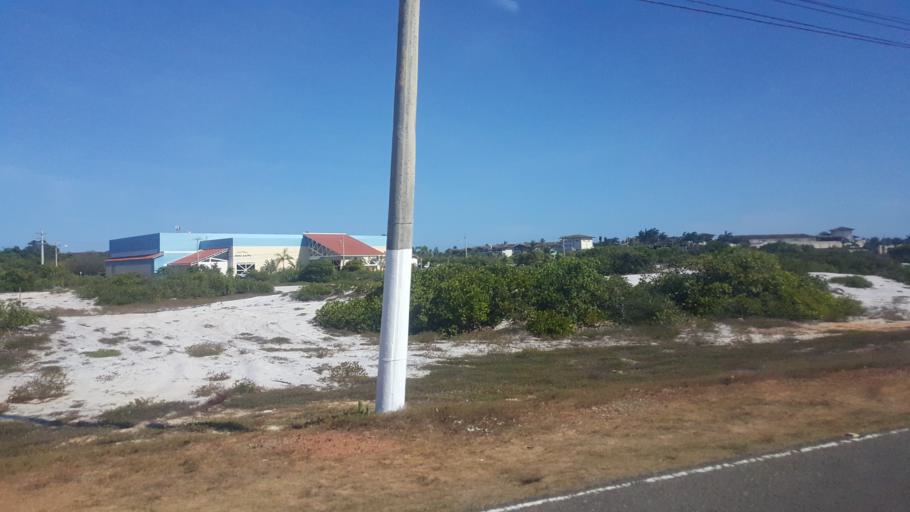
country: BR
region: Bahia
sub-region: Mata De Sao Joao
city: Mata de Sao Joao
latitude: -12.4361
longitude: -37.9209
